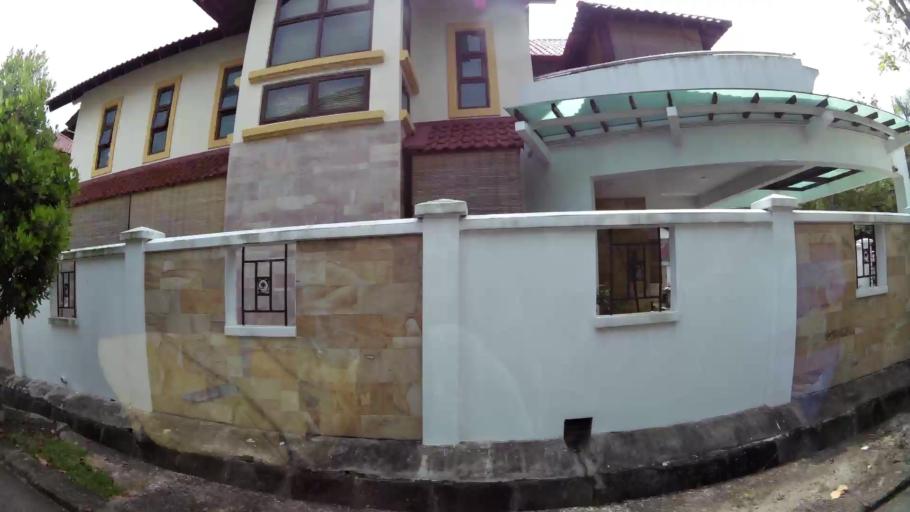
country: SG
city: Singapore
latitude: 1.3239
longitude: 103.7677
